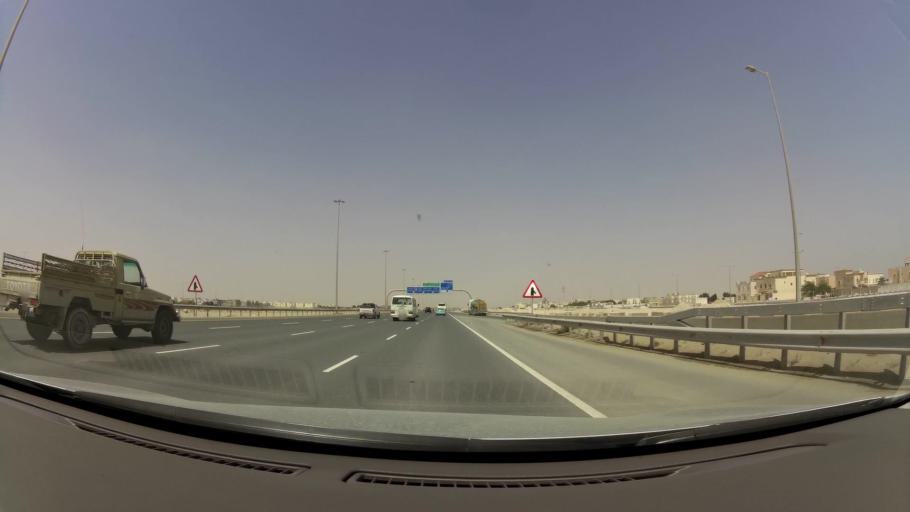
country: QA
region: Baladiyat Umm Salal
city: Umm Salal `Ali
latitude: 25.4730
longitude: 51.4081
